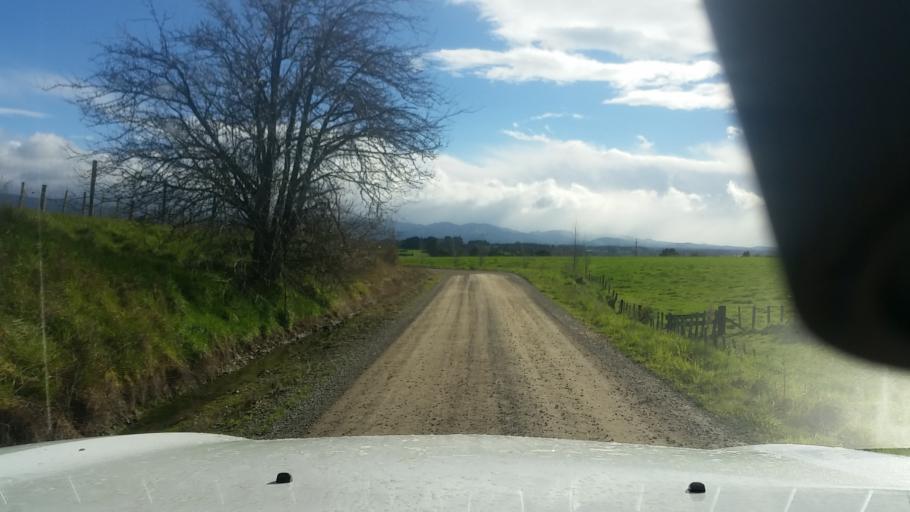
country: NZ
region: Wellington
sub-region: Masterton District
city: Masterton
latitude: -41.1443
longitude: 175.4727
